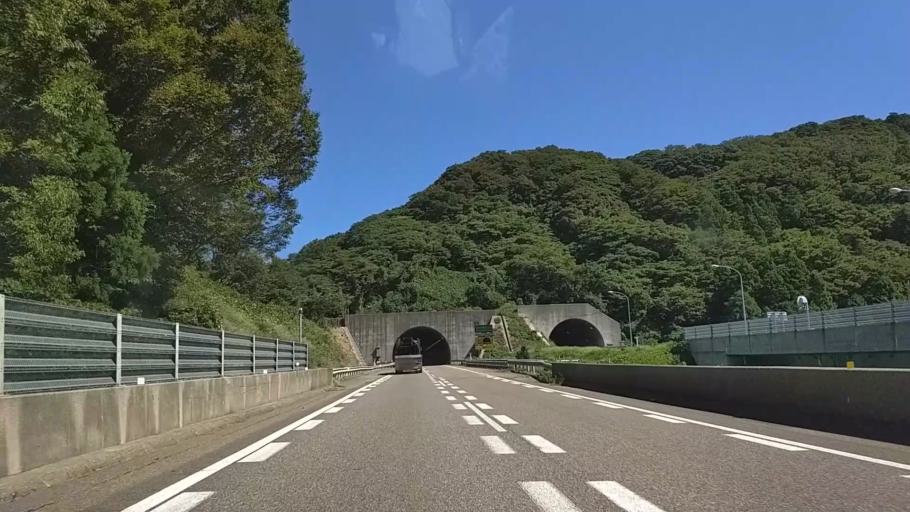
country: JP
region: Niigata
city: Joetsu
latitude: 37.1430
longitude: 138.0653
